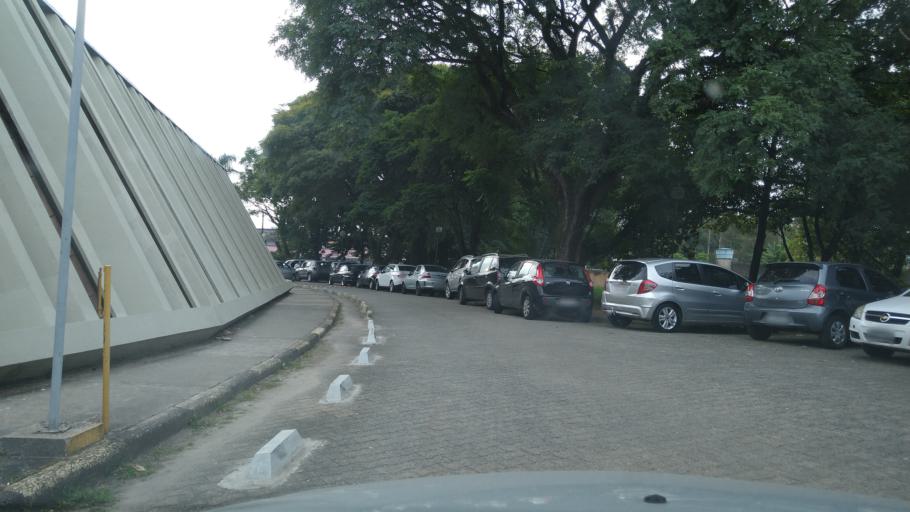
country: BR
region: Sao Paulo
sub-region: Sao Paulo
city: Sao Paulo
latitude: -23.5314
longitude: -46.5988
